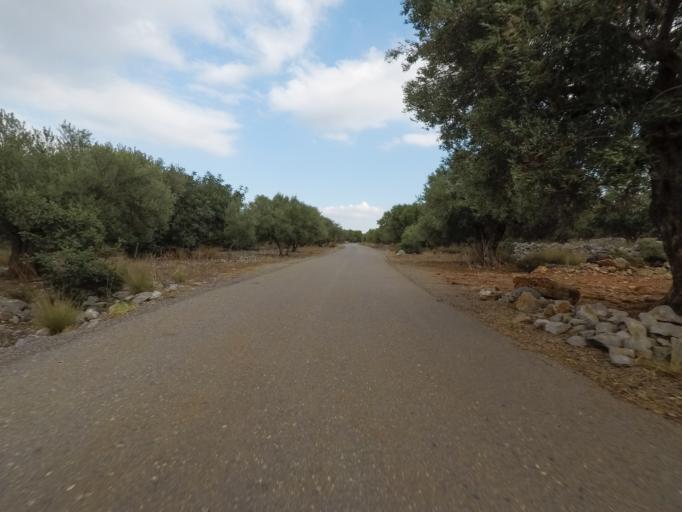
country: GR
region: Crete
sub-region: Nomos Lasithiou
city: Kritsa
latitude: 35.1749
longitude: 25.6525
